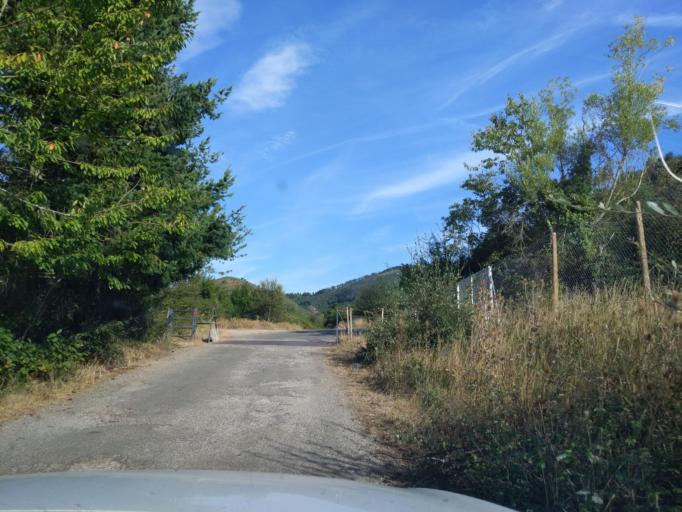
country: ES
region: La Rioja
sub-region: Provincia de La Rioja
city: Ezcaray
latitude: 42.3226
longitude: -3.0211
